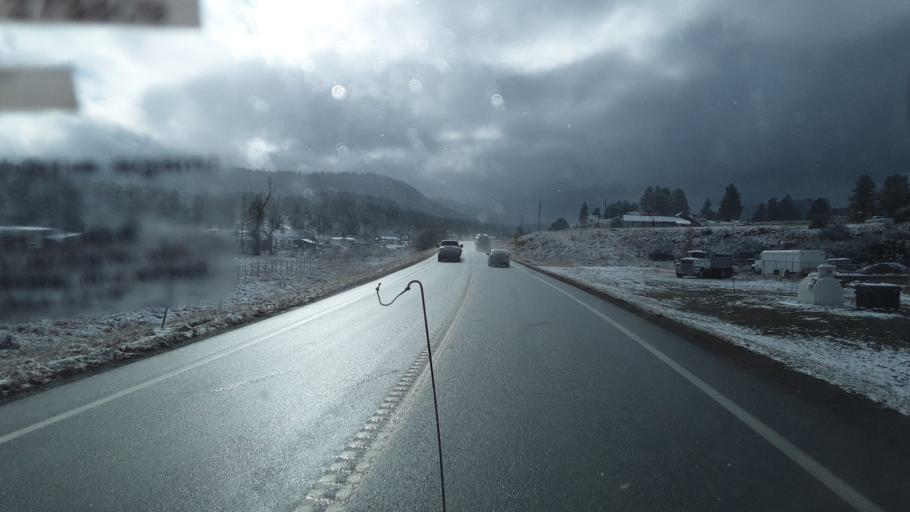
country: US
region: Colorado
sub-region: Archuleta County
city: Pagosa Springs
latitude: 37.2362
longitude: -107.1760
